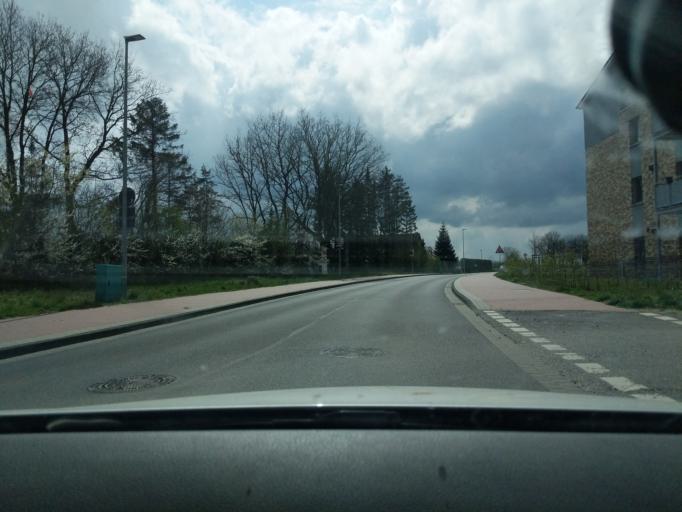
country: DE
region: Lower Saxony
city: Stade
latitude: 53.5696
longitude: 9.4709
